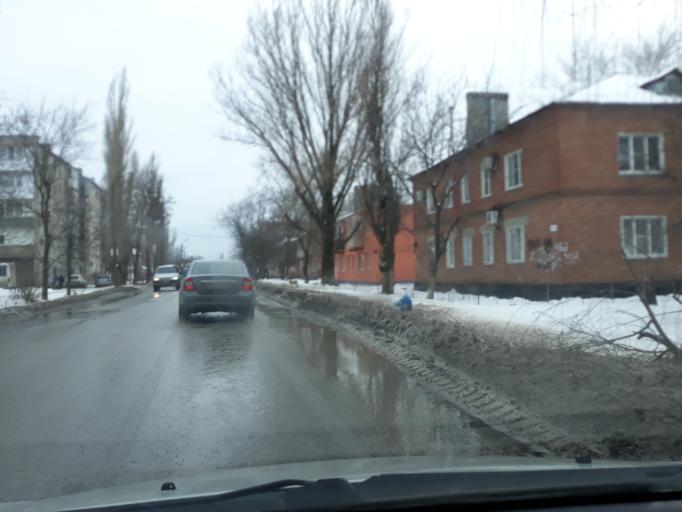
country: RU
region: Rostov
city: Taganrog
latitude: 47.2350
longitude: 38.8766
